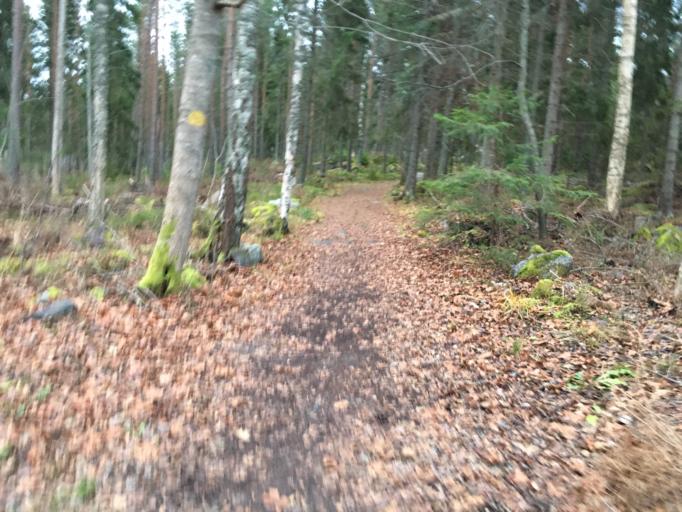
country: SE
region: Uppsala
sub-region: Alvkarleby Kommun
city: AElvkarleby
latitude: 60.6494
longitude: 17.5532
